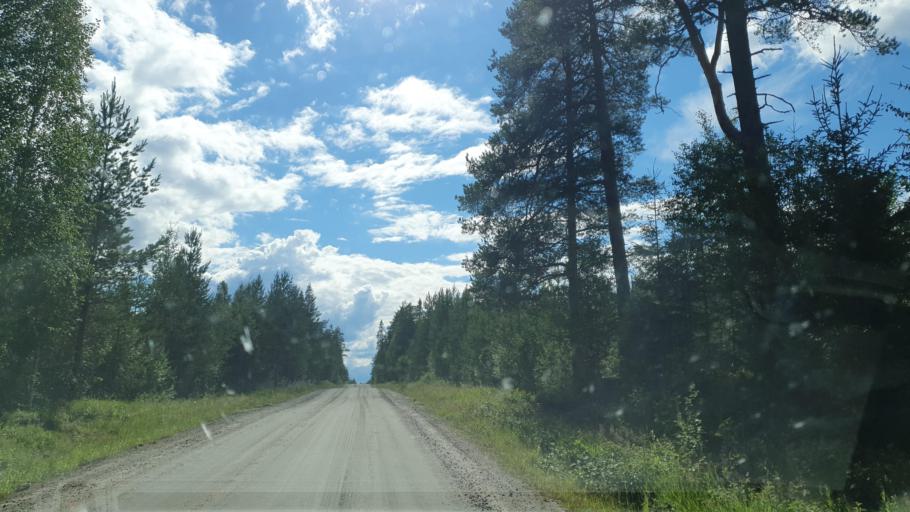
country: FI
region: Kainuu
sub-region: Kehys-Kainuu
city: Kuhmo
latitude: 64.1492
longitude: 29.7238
